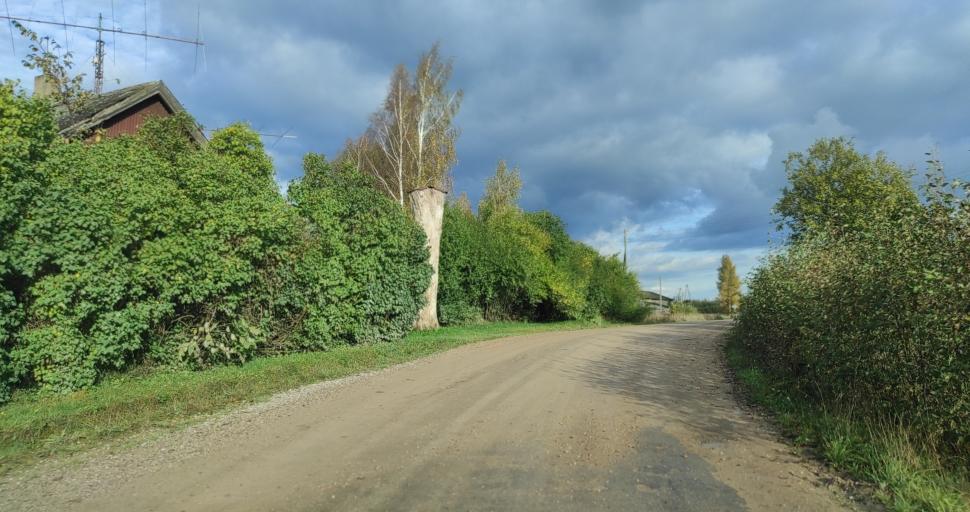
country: LV
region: Aizpute
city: Aizpute
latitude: 56.8036
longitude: 21.6640
